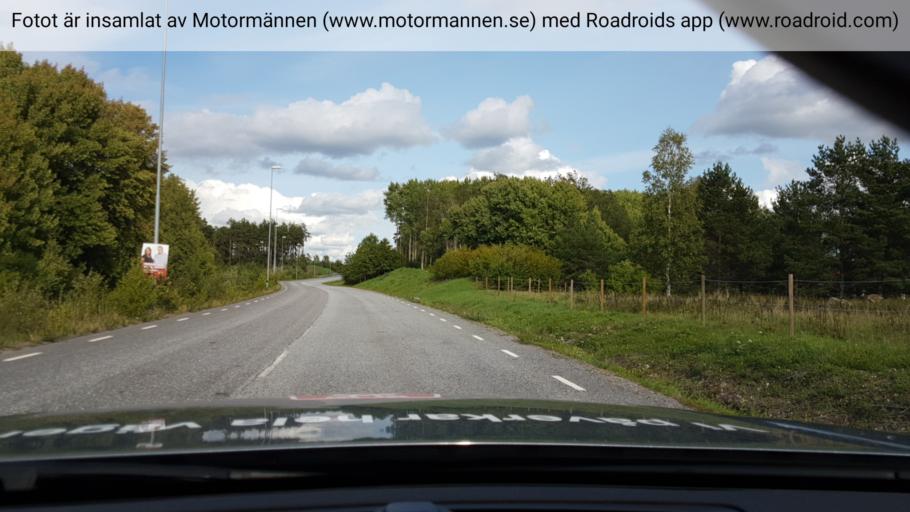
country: SE
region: Stockholm
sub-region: Upplands-Bro Kommun
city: Bro
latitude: 59.5068
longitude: 17.6623
